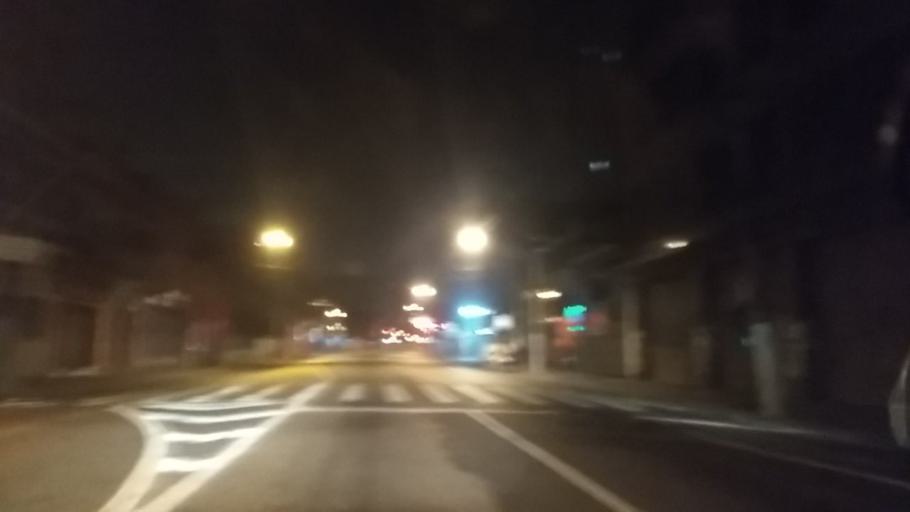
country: BR
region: Sao Paulo
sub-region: Sao Paulo
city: Sao Paulo
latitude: -23.5395
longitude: -46.6096
